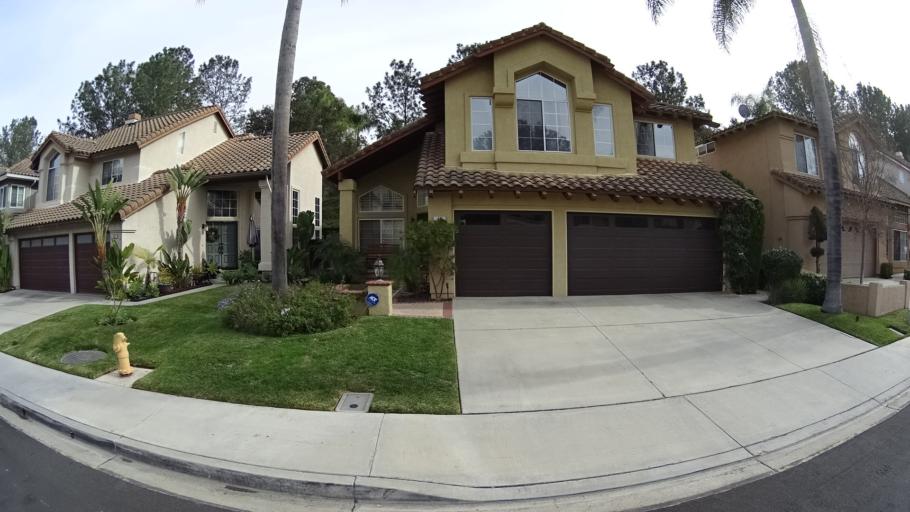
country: US
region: California
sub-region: Orange County
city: Laguna Woods
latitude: 33.5998
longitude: -117.7413
